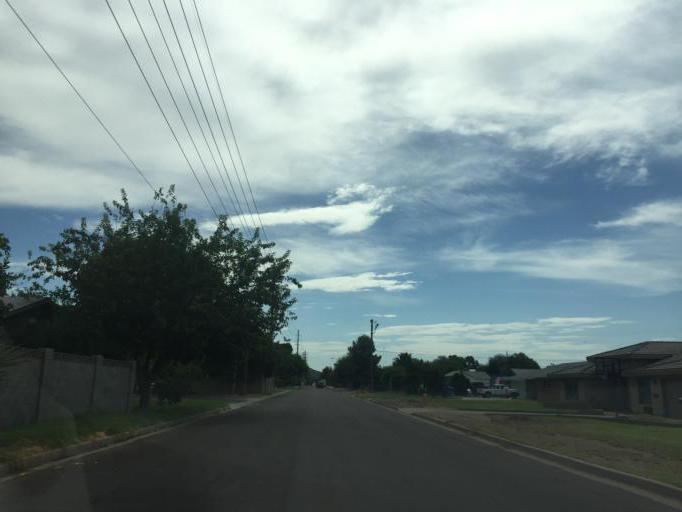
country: US
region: Arizona
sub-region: Maricopa County
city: Phoenix
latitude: 33.5346
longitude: -112.0594
